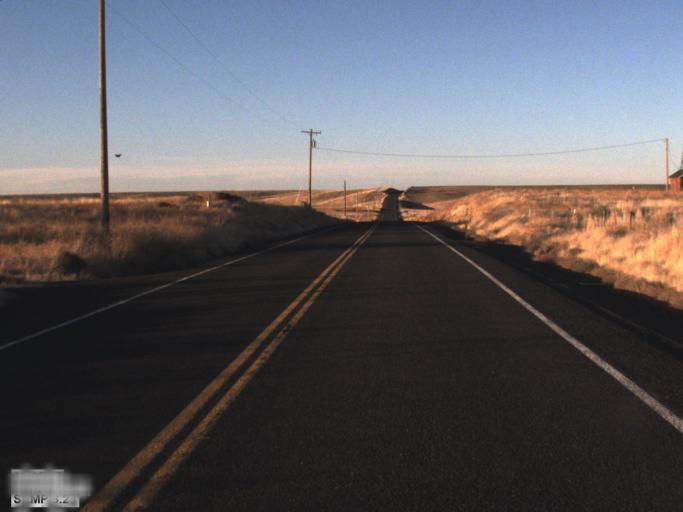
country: US
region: Washington
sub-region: Franklin County
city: Connell
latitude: 46.7167
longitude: -118.5481
